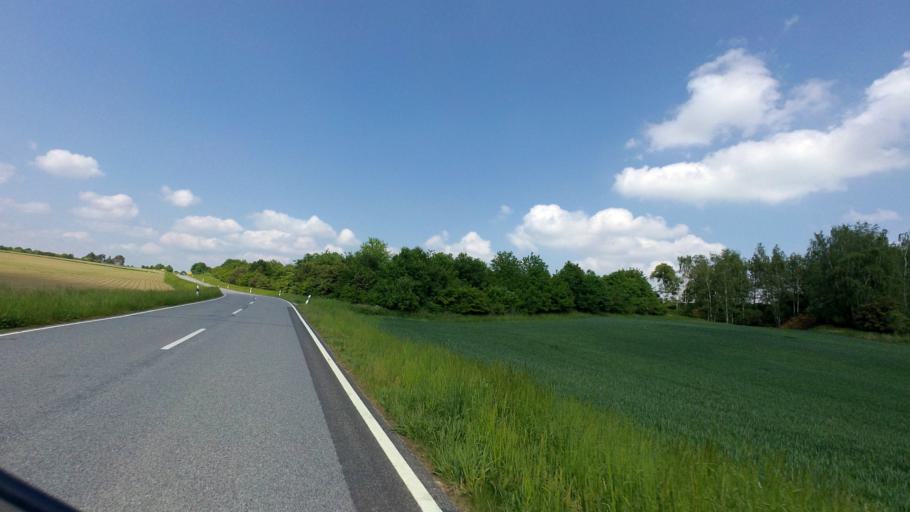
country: DE
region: Saxony
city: Weissenberg
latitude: 51.2040
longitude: 14.6050
